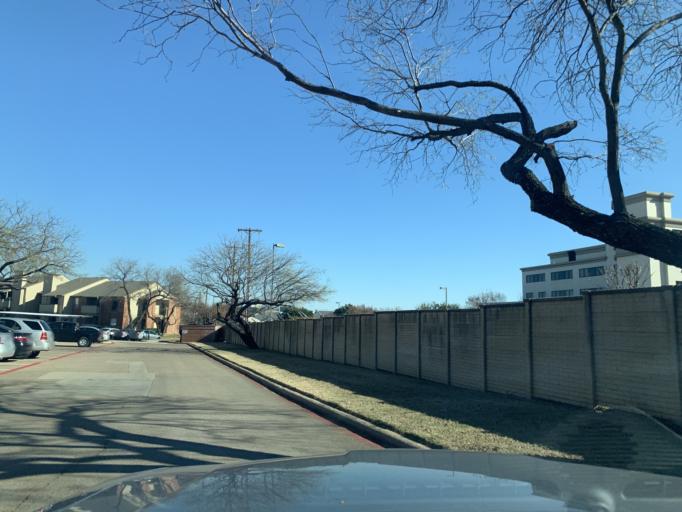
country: US
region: Texas
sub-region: Tarrant County
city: Bedford
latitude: 32.8398
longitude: -97.1472
